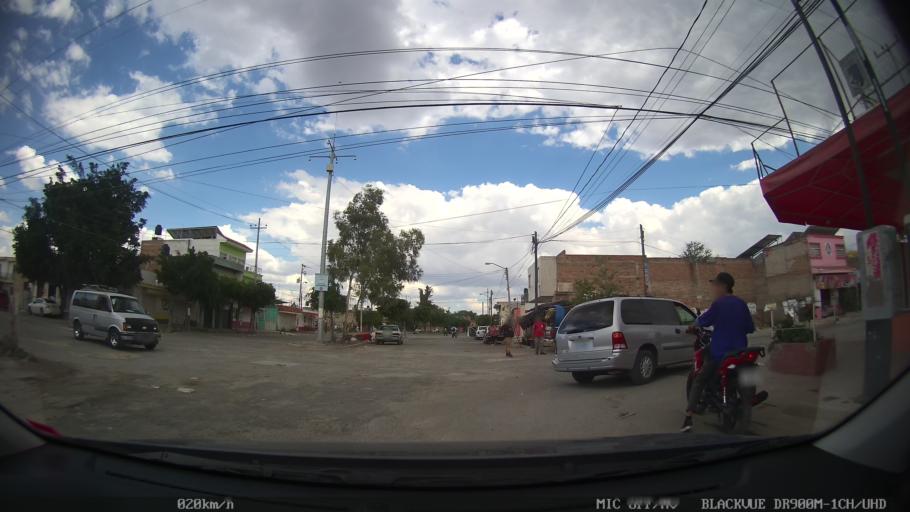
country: MX
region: Jalisco
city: Tonala
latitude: 20.6637
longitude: -103.2515
